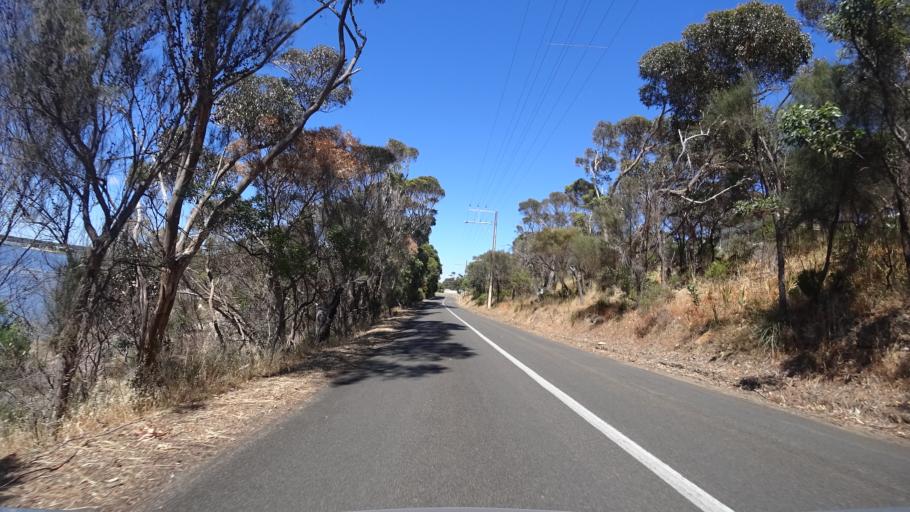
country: AU
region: South Australia
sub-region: Kangaroo Island
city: Kingscote
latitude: -35.7804
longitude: 137.7721
